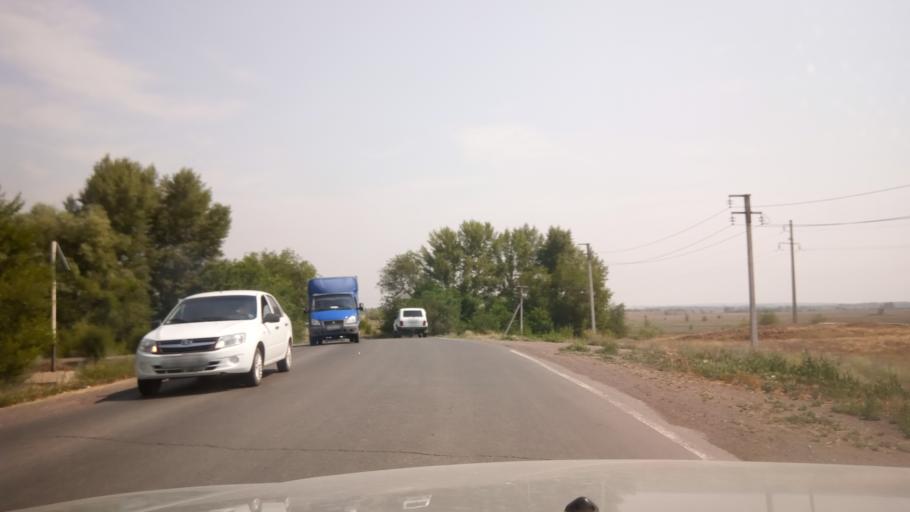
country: RU
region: Orenburg
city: Novotroitsk
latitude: 51.1704
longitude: 58.2621
